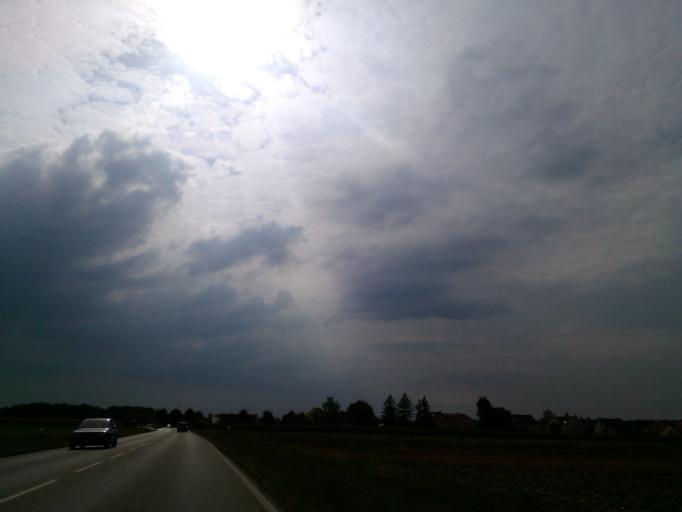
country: DE
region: Bavaria
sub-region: Upper Bavaria
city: Puchheim
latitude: 48.1594
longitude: 11.3379
